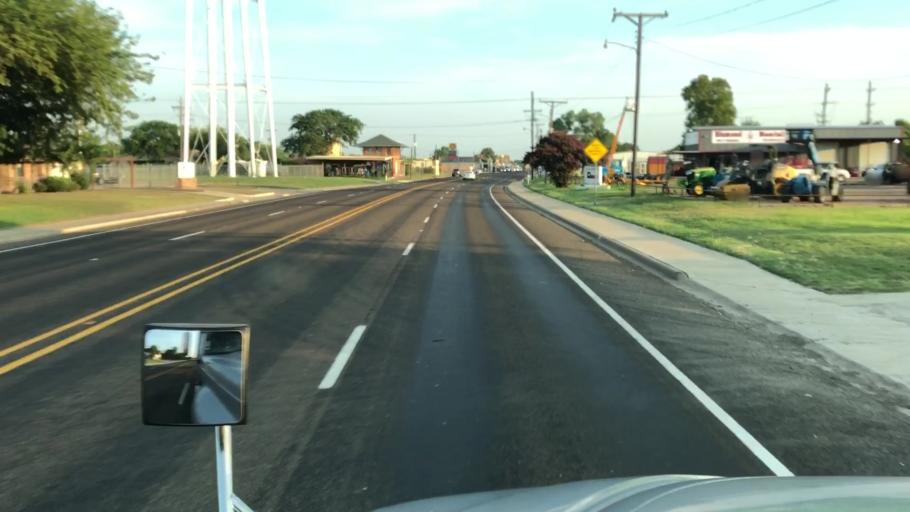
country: US
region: Texas
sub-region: Robertson County
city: Calvert
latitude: 30.9748
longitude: -96.6709
